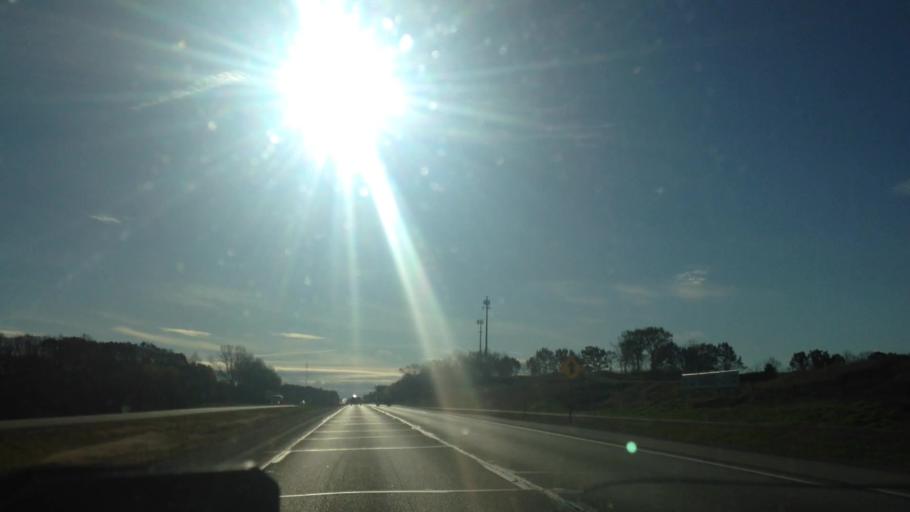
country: US
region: Wisconsin
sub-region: Washington County
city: Slinger
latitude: 43.3458
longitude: -88.2802
